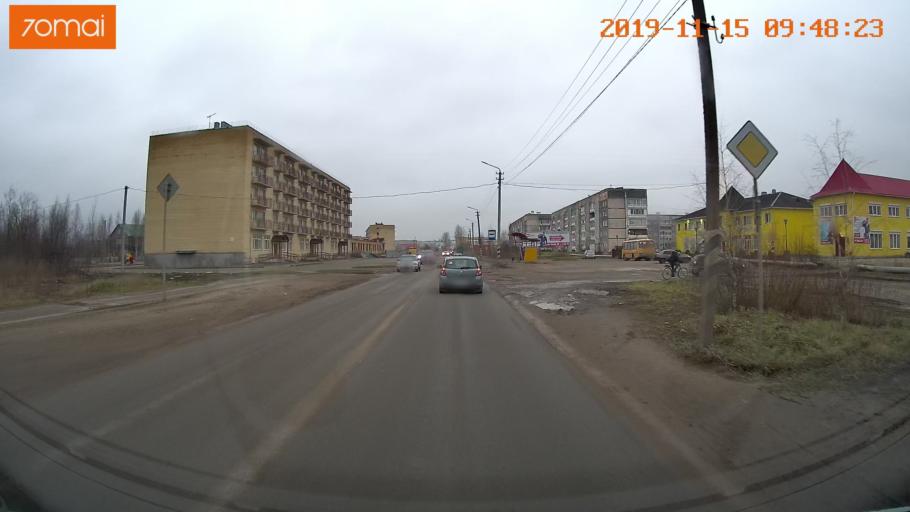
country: RU
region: Vologda
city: Sheksna
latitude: 59.2228
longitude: 38.5127
